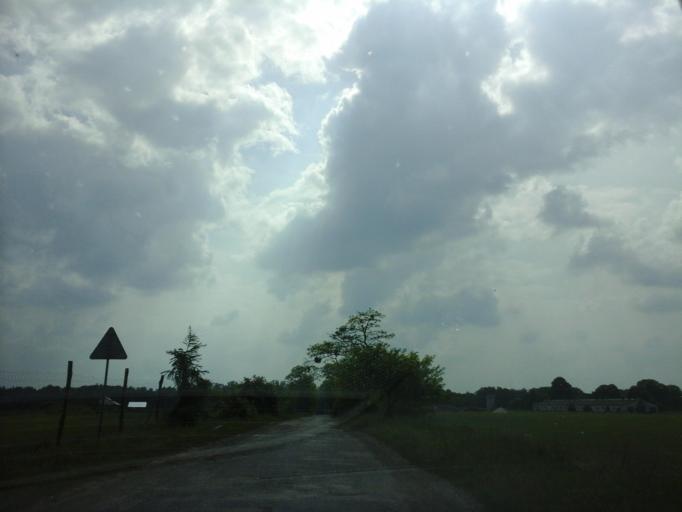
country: PL
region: West Pomeranian Voivodeship
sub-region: Powiat choszczenski
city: Drawno
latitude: 53.1834
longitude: 15.8634
